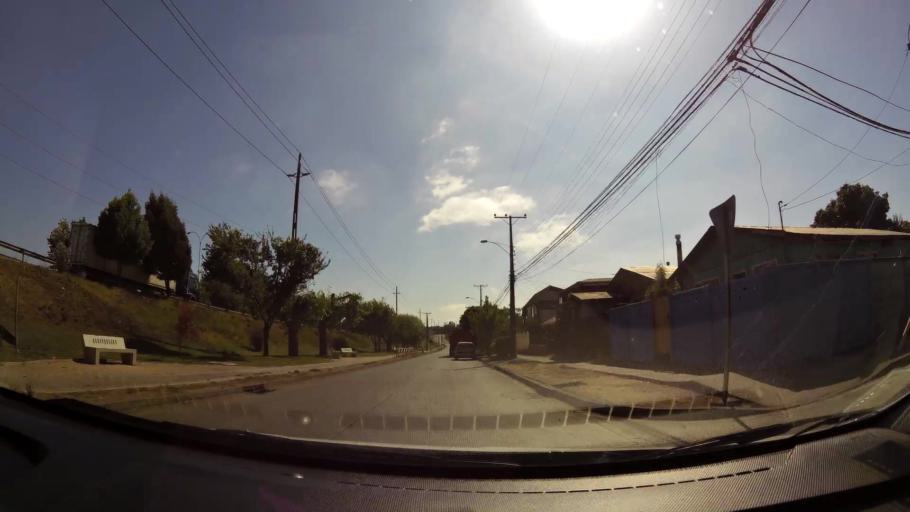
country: CL
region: Biobio
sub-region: Provincia de Concepcion
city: Concepcion
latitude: -36.7988
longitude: -73.0493
